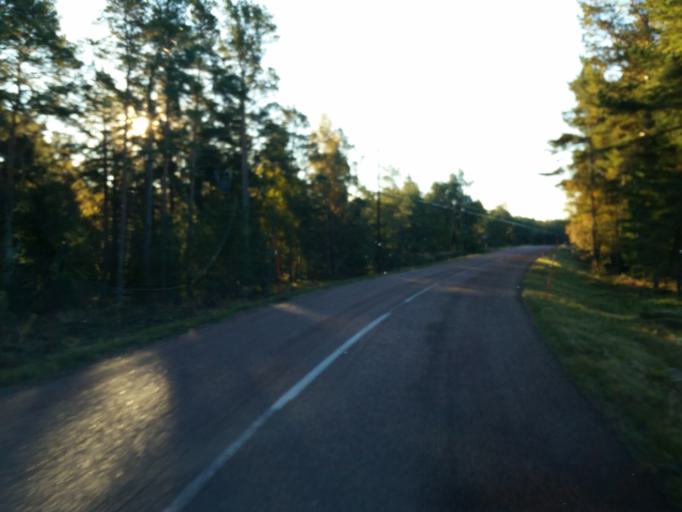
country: AX
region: Alands skaergard
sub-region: Vardoe
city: Vardoe
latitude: 60.3086
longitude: 20.3795
